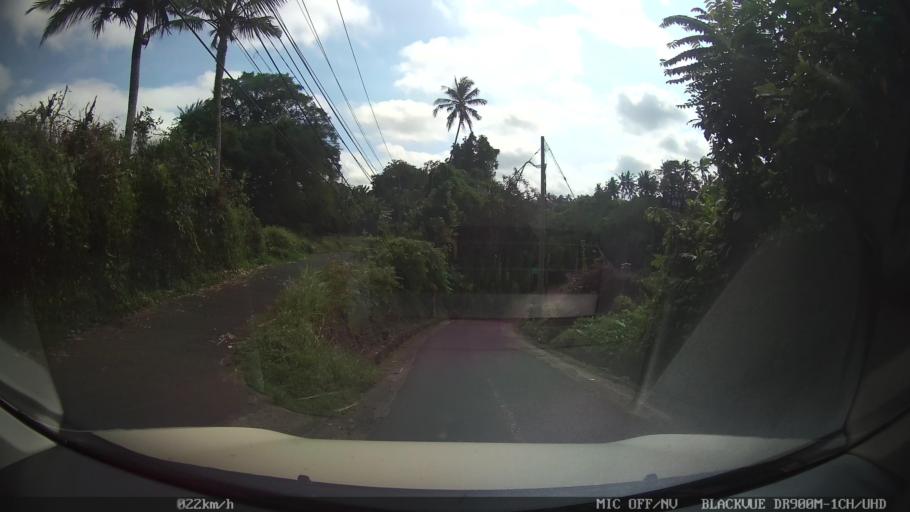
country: ID
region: Bali
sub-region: Kabupaten Gianyar
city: Ubud
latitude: -8.5079
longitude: 115.2812
